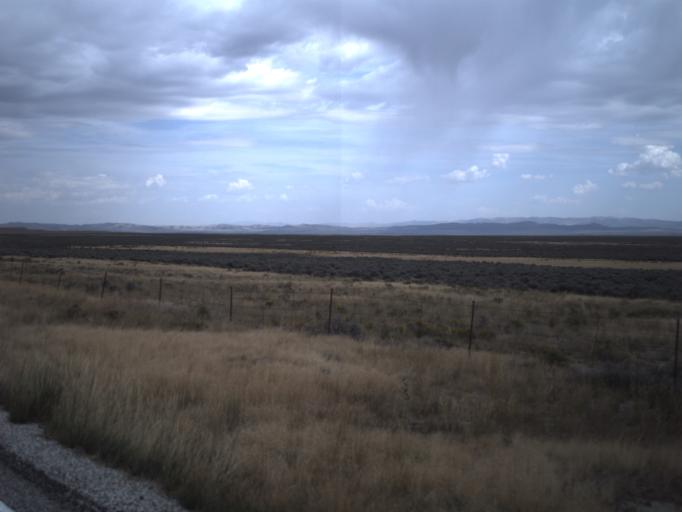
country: US
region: Idaho
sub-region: Oneida County
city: Malad City
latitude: 41.9286
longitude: -113.0908
